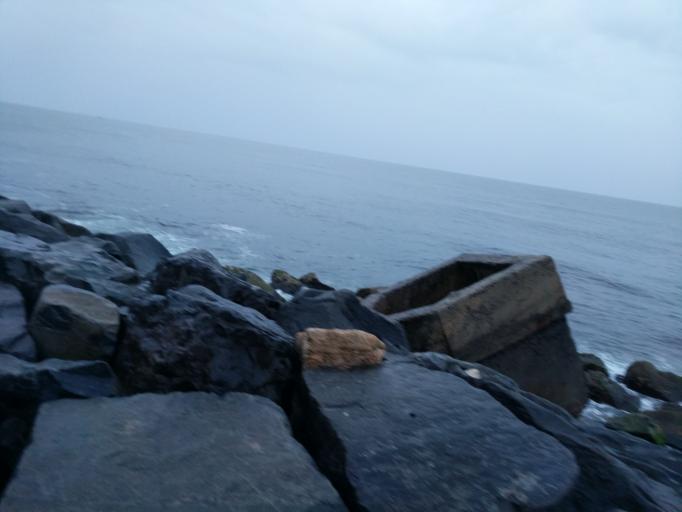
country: US
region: New York
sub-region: Suffolk County
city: Montauk
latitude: 41.0704
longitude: -71.8572
